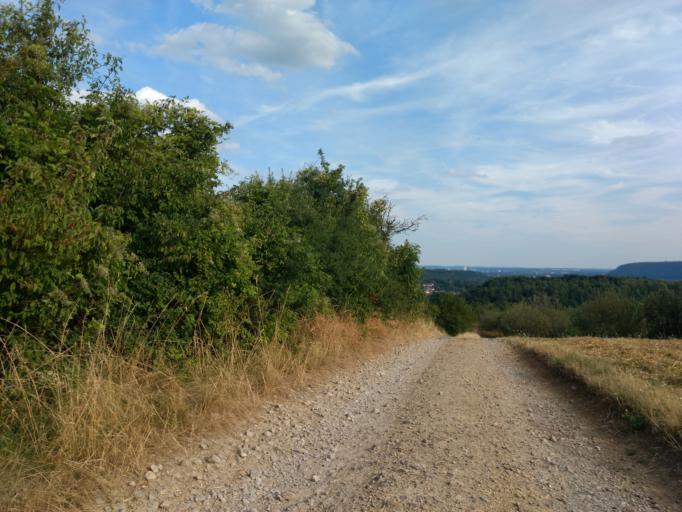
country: DE
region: Saarland
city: Beckingen
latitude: 49.3990
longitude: 6.6954
